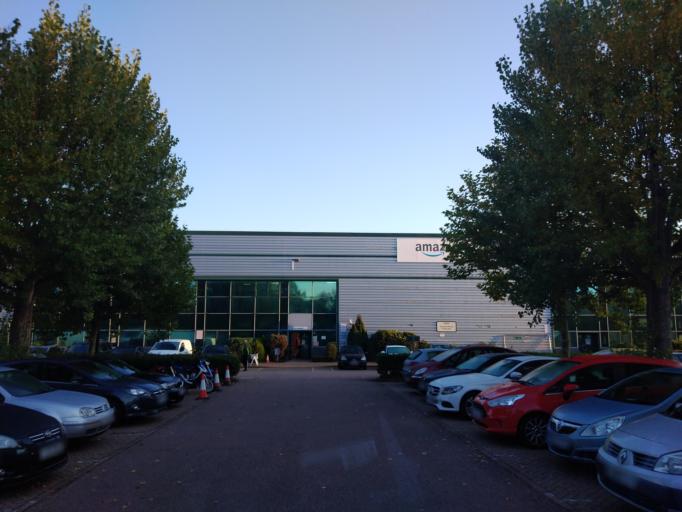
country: GB
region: England
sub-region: West Sussex
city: Littlehampton
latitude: 50.8214
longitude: -0.5287
